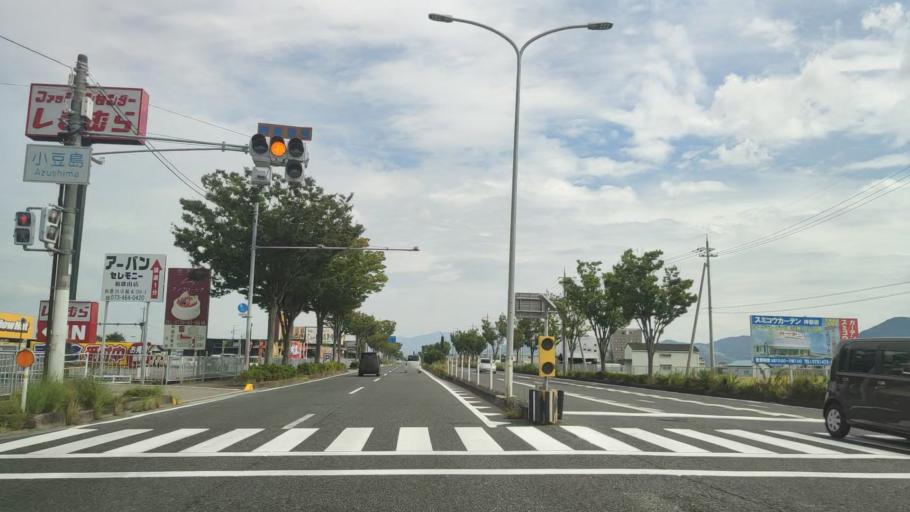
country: JP
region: Wakayama
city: Wakayama-shi
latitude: 34.2557
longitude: 135.2325
